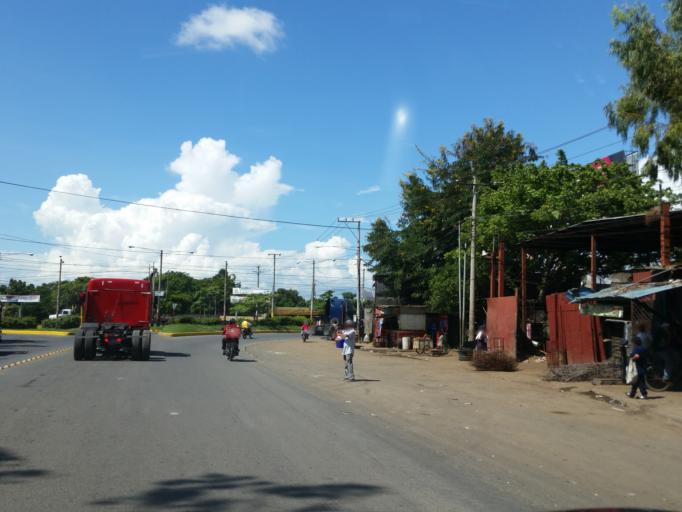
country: NI
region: Managua
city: Managua
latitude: 12.1470
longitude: -86.1952
